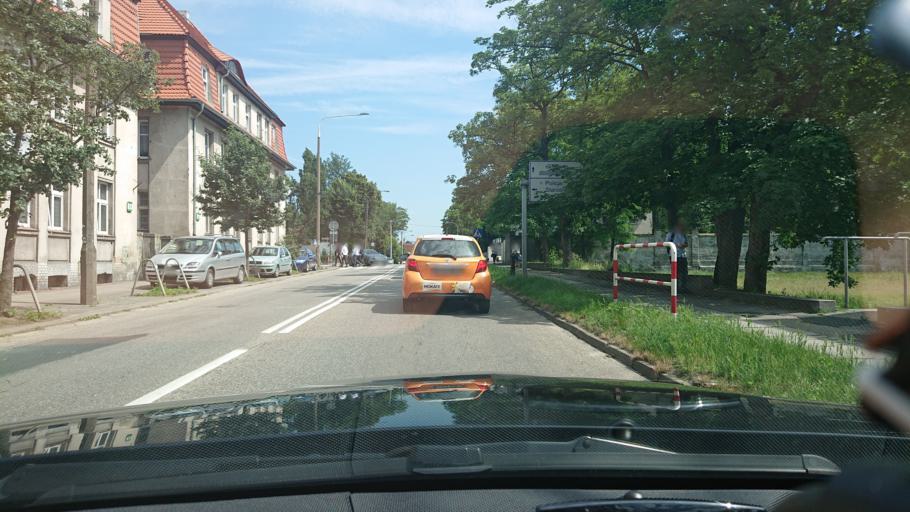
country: PL
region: Greater Poland Voivodeship
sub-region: Powiat gnieznienski
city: Gniezno
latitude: 52.5347
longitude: 17.6053
